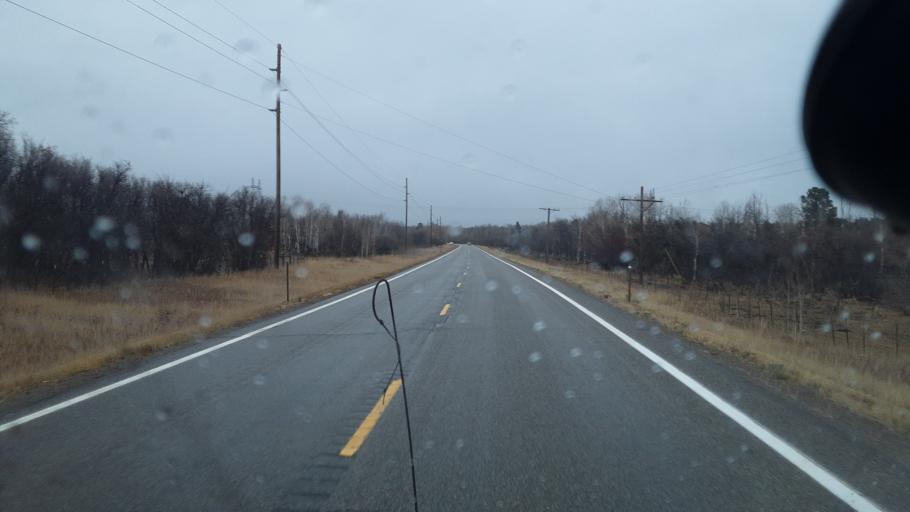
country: US
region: Colorado
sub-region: La Plata County
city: Durango
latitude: 37.2394
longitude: -108.0405
